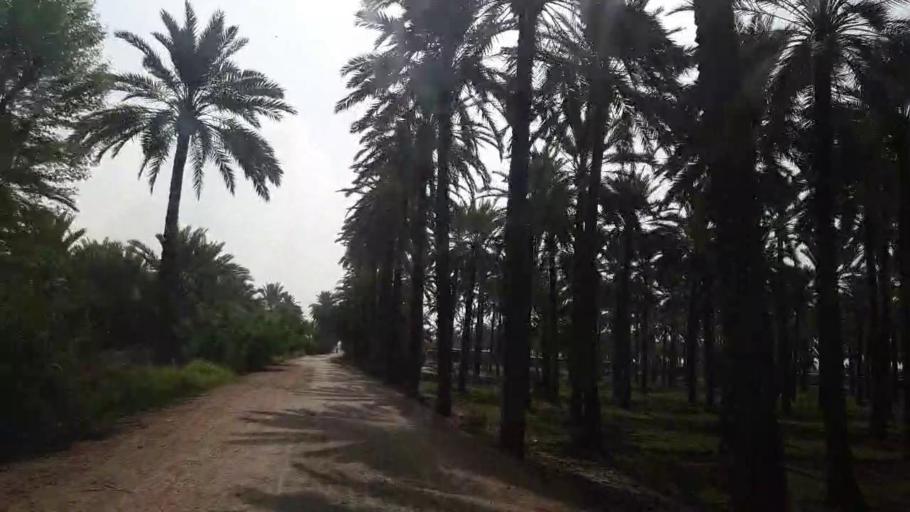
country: PK
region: Sindh
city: Khairpur
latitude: 27.5704
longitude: 68.7530
